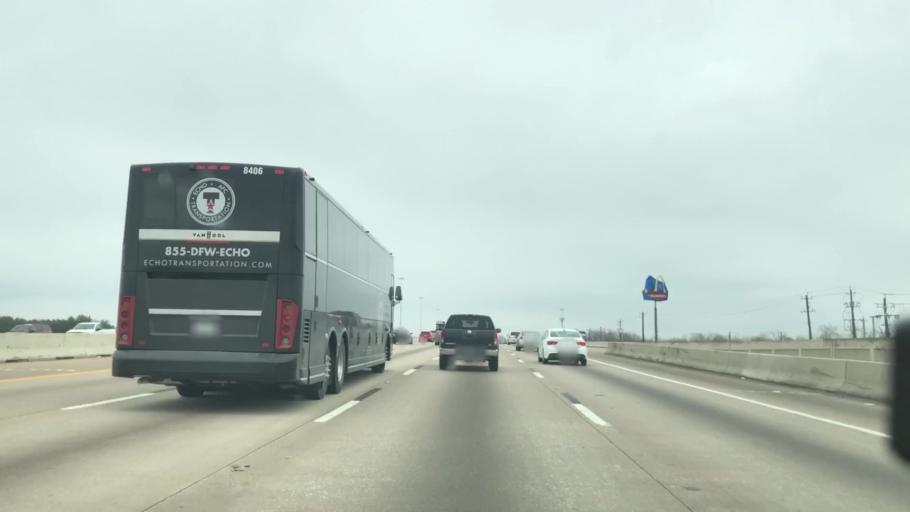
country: US
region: Texas
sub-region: Harris County
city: Aldine
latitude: 29.8698
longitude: -95.3294
